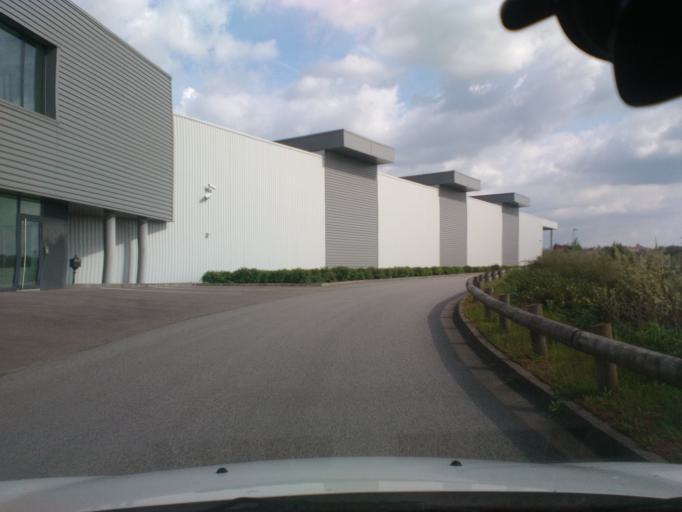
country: FR
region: Lorraine
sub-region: Departement des Vosges
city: Mirecourt
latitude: 48.3303
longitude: 6.1446
